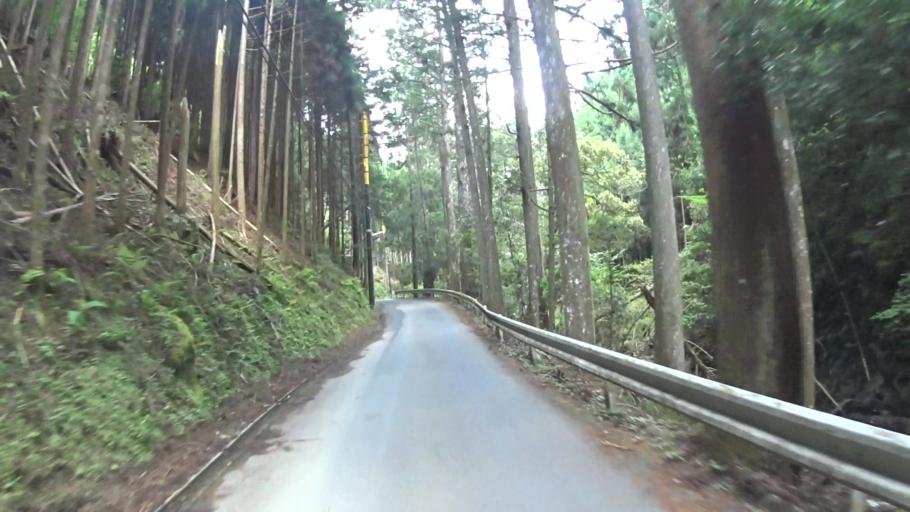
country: JP
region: Kyoto
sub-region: Kyoto-shi
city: Kamigyo-ku
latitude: 35.1023
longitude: 135.7033
